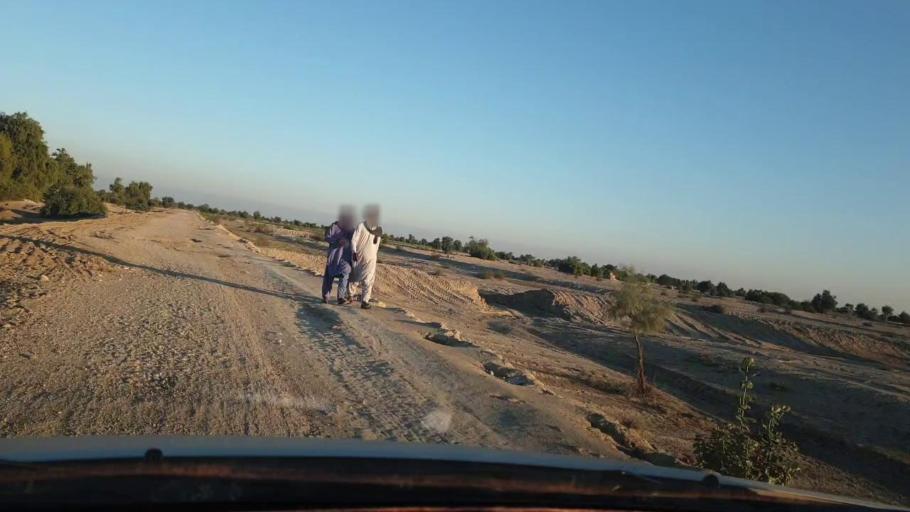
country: PK
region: Sindh
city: Johi
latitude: 26.8071
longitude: 67.4767
